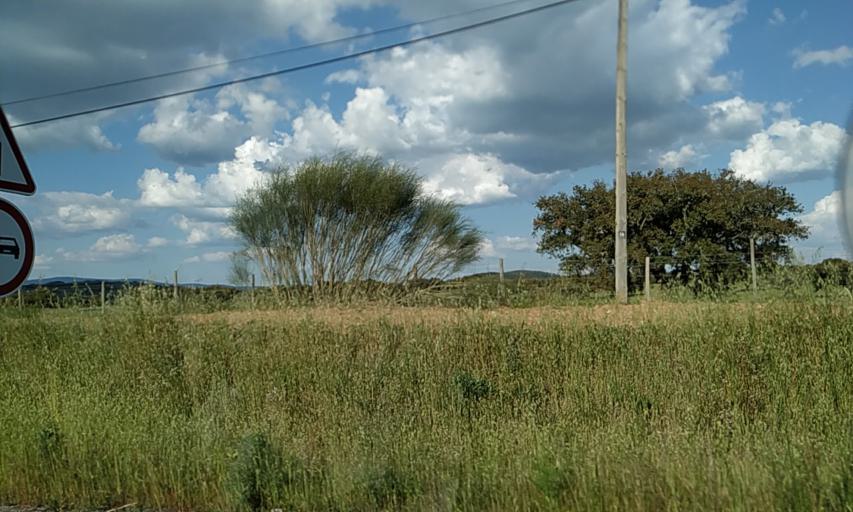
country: PT
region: Portalegre
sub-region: Portalegre
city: Urra
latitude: 39.1938
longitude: -7.4571
